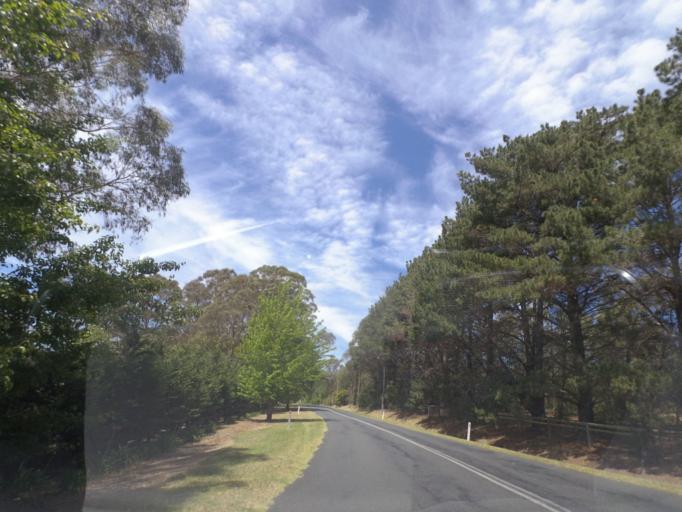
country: AU
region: New South Wales
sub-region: Wingecarribee
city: Colo Vale
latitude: -34.4103
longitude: 150.5201
